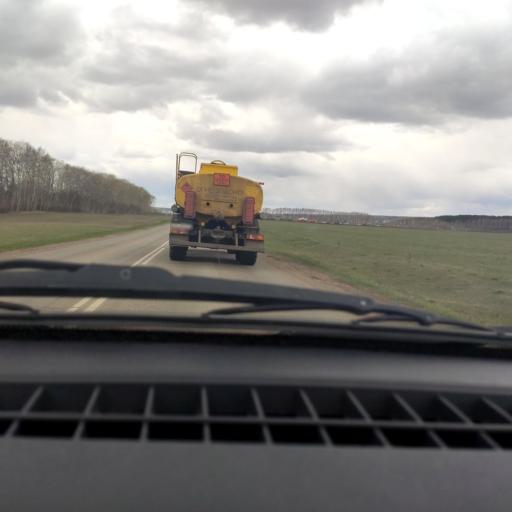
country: RU
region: Bashkortostan
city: Chekmagush
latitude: 55.1278
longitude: 54.6952
